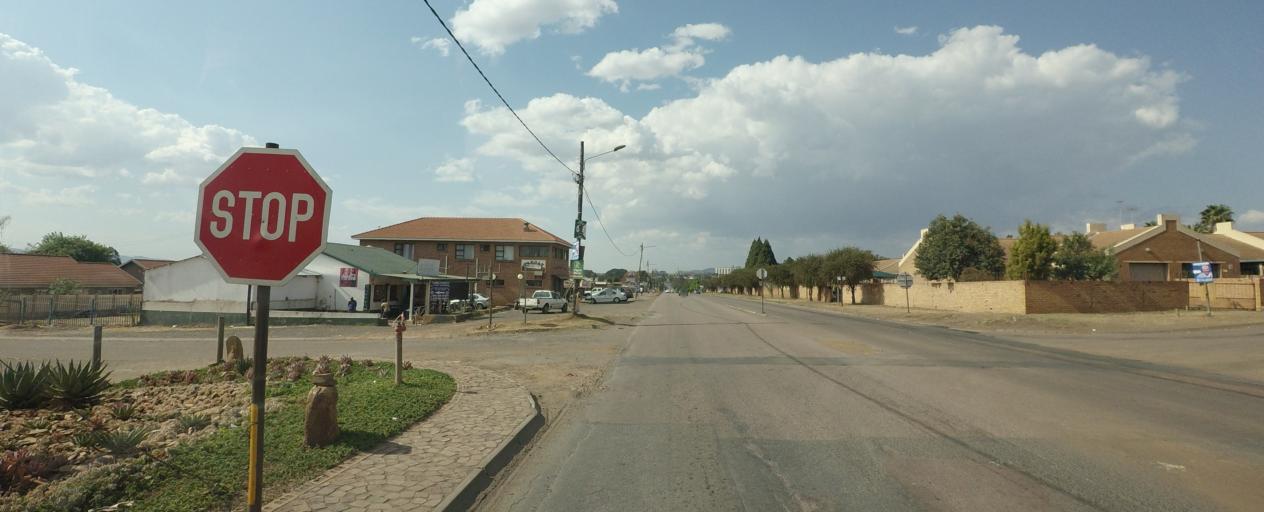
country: ZA
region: Mpumalanga
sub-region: Ehlanzeni District
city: Lydenburg
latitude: -25.1071
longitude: 30.4502
